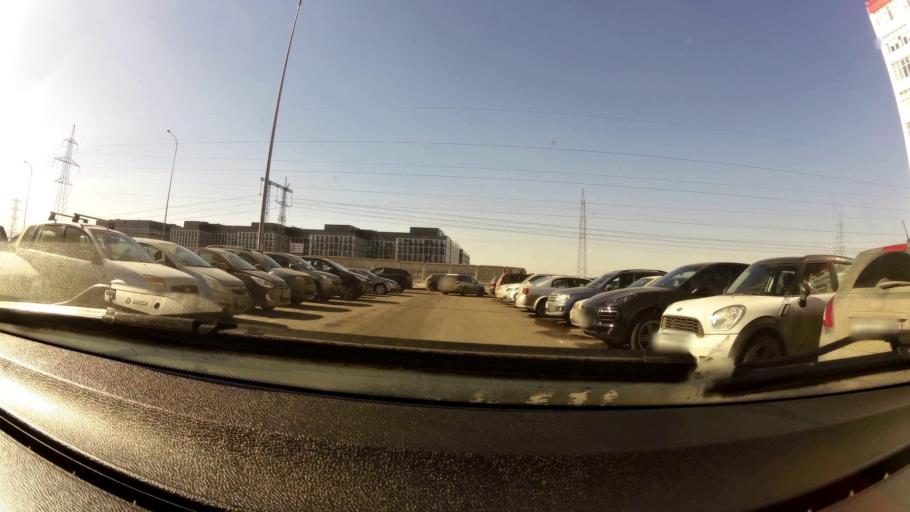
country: RU
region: Moskovskaya
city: Mosrentgen
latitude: 55.6365
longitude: 37.4353
